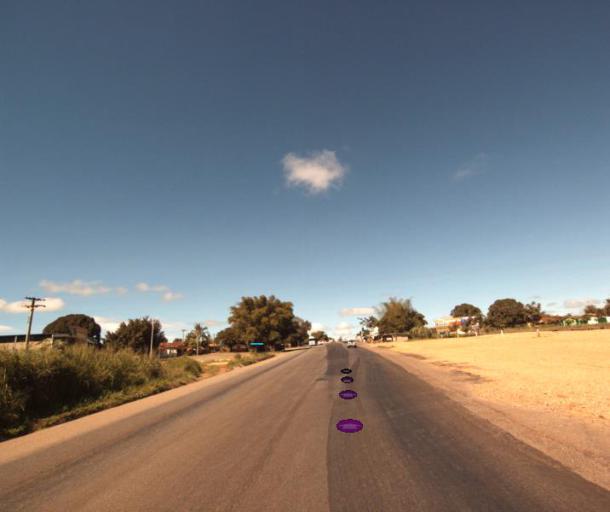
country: BR
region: Goias
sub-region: Ceres
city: Ceres
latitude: -15.1703
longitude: -49.5440
